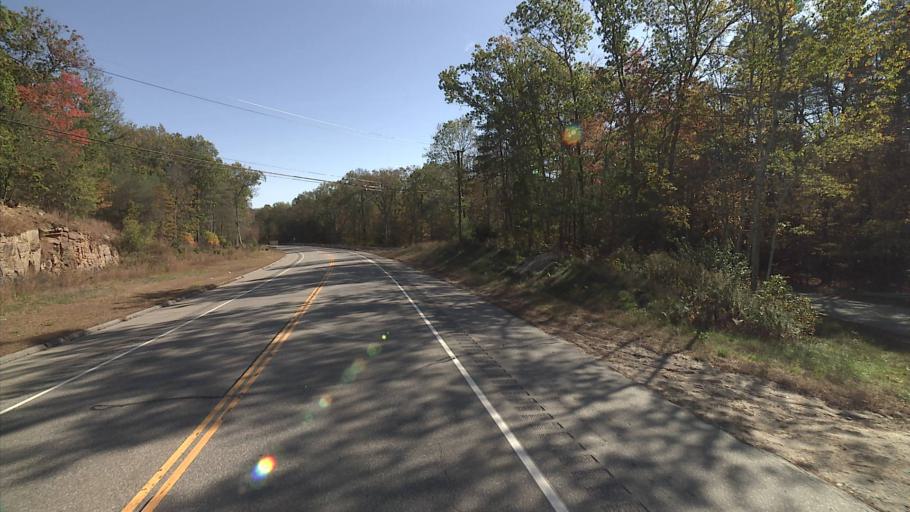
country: US
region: Connecticut
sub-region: Windham County
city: Danielson
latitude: 41.7898
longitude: -71.8686
